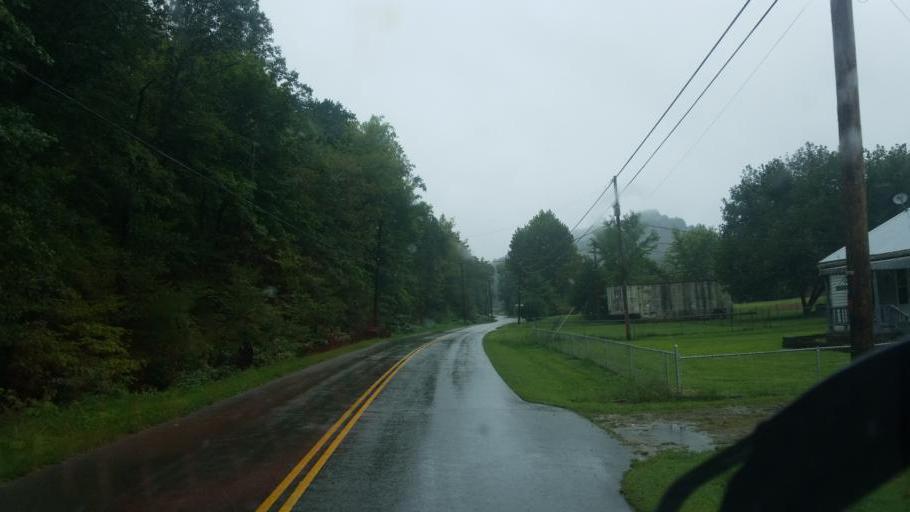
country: US
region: Ohio
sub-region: Scioto County
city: West Portsmouth
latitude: 38.7394
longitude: -83.0719
